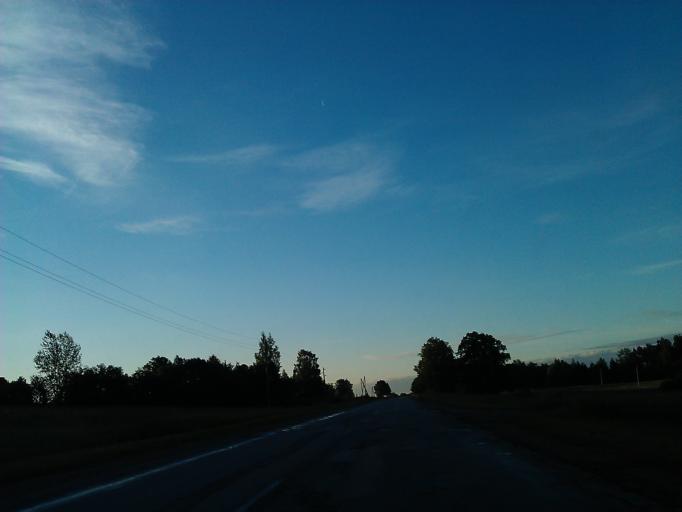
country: LV
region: Pargaujas
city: Stalbe
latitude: 57.3430
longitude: 25.1291
